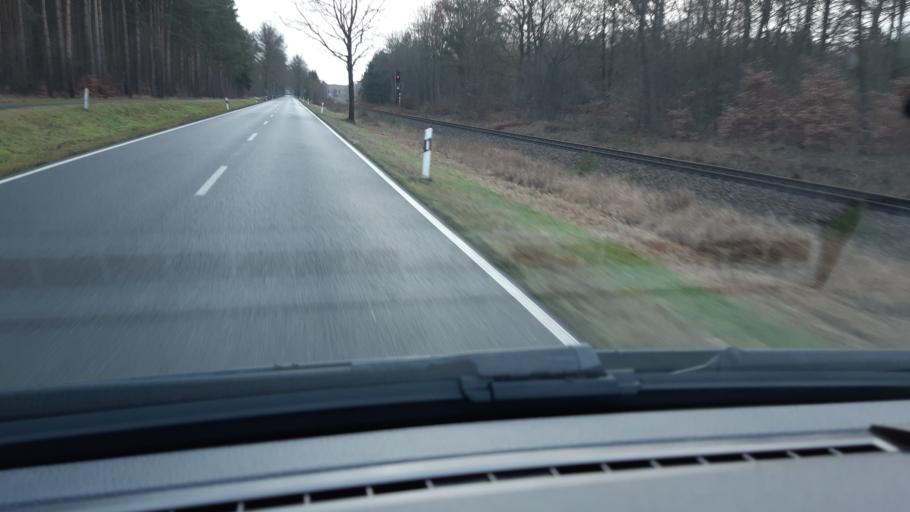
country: DE
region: Brandenburg
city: Zehdenick
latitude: 53.0432
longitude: 13.3900
